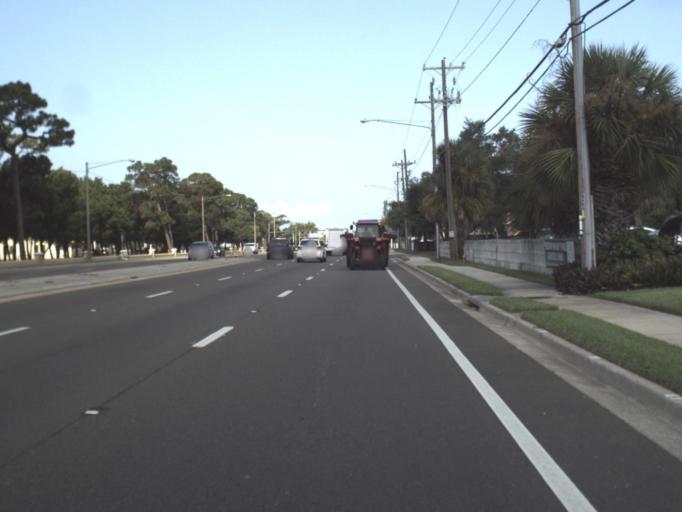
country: US
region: Florida
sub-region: Pinellas County
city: Bay Pines
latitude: 27.8140
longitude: -82.7748
